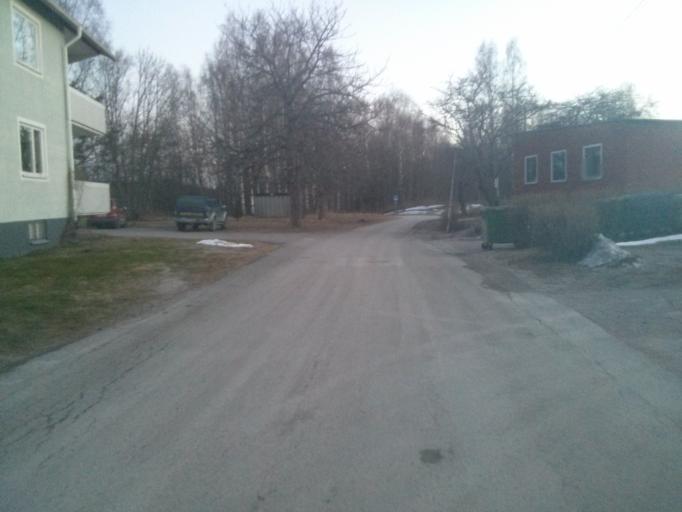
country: SE
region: Vaesternorrland
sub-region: Sundsvalls Kommun
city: Kvissleby
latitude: 62.2944
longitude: 17.3811
